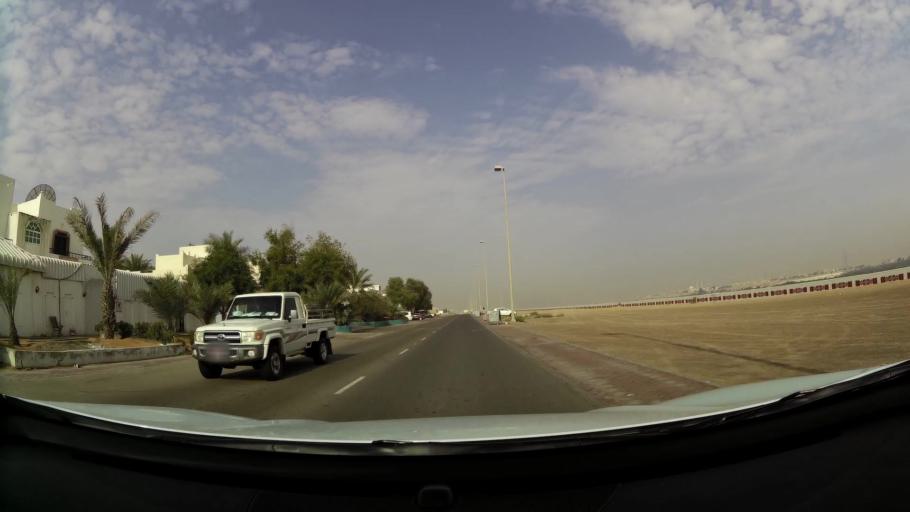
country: AE
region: Abu Dhabi
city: Abu Dhabi
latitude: 24.2442
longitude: 54.7135
